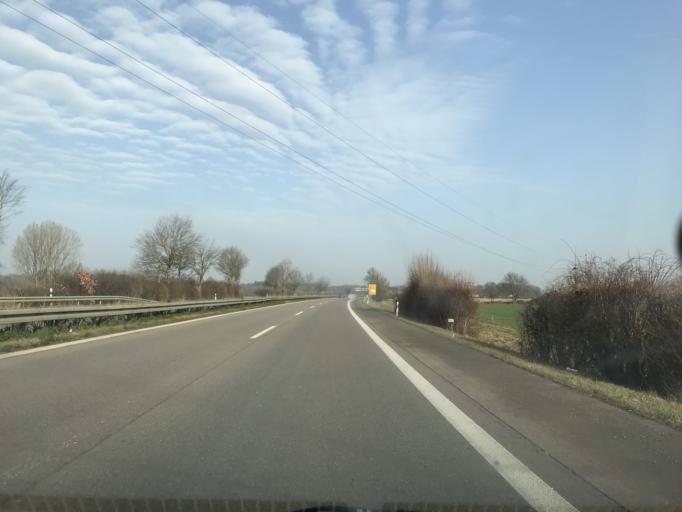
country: DE
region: Baden-Wuerttemberg
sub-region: Freiburg Region
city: Ebringen
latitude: 47.9739
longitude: 7.7715
